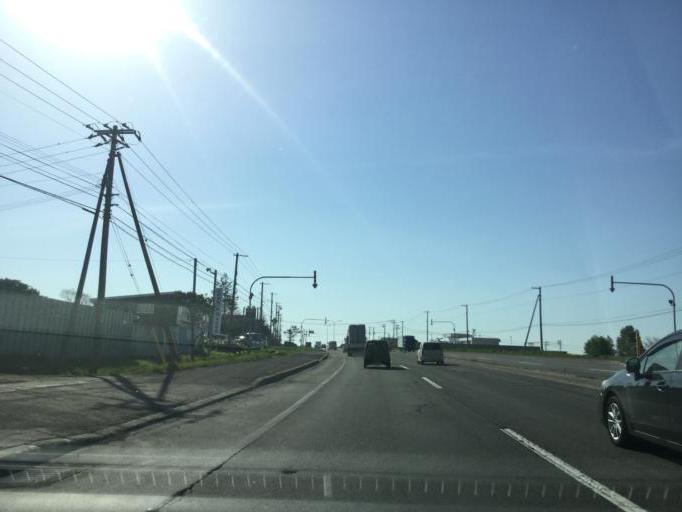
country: JP
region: Hokkaido
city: Kitahiroshima
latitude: 43.0069
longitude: 141.5230
